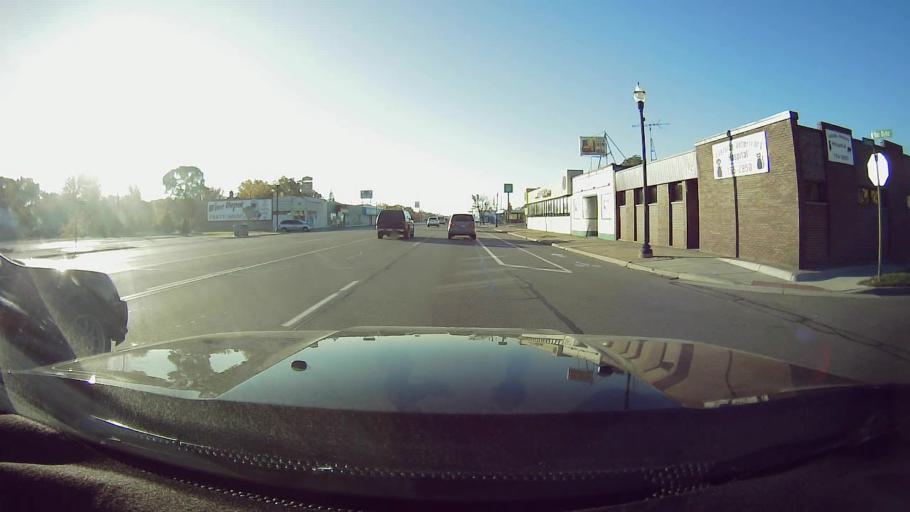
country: US
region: Michigan
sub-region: Macomb County
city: Warren
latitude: 42.4686
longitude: -83.0270
